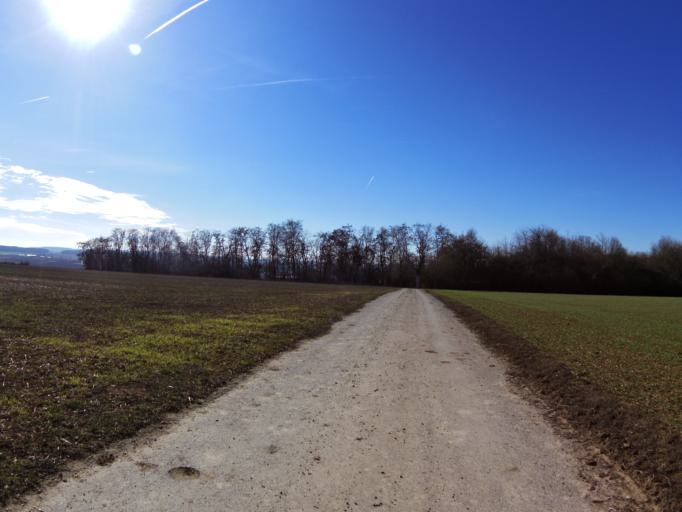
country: DE
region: Bavaria
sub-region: Regierungsbezirk Unterfranken
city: Kurnach
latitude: 49.8476
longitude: 10.0164
